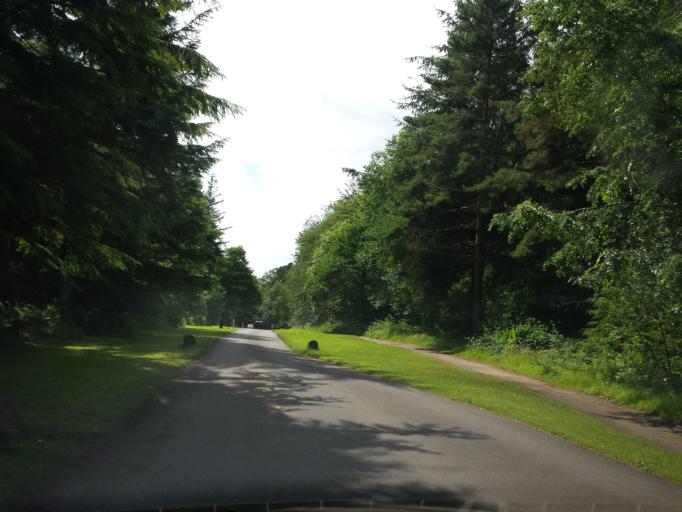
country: GB
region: Scotland
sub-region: South Ayrshire
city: Maybole
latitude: 55.3502
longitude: -4.7940
